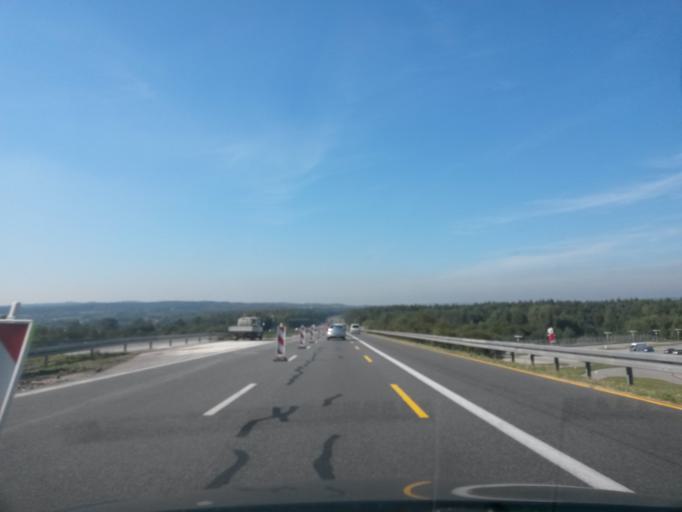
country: PL
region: Lesser Poland Voivodeship
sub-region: Powiat chrzanowski
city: Grojec
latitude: 50.1009
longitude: 19.5476
